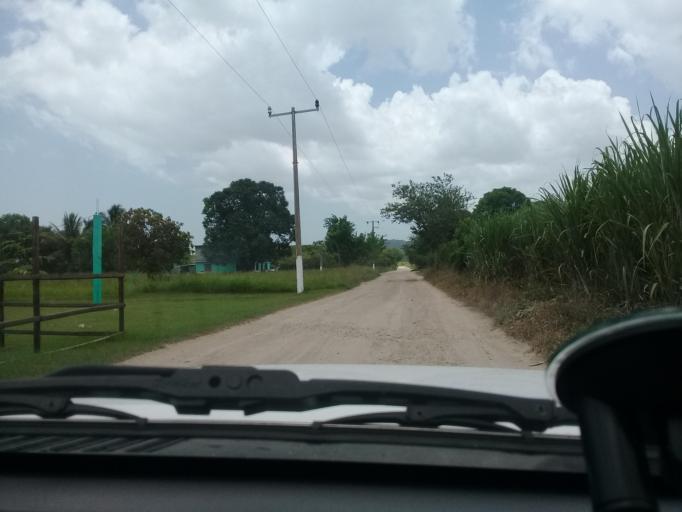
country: MX
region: Veracruz
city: Panuco
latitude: 22.1278
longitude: -98.0560
